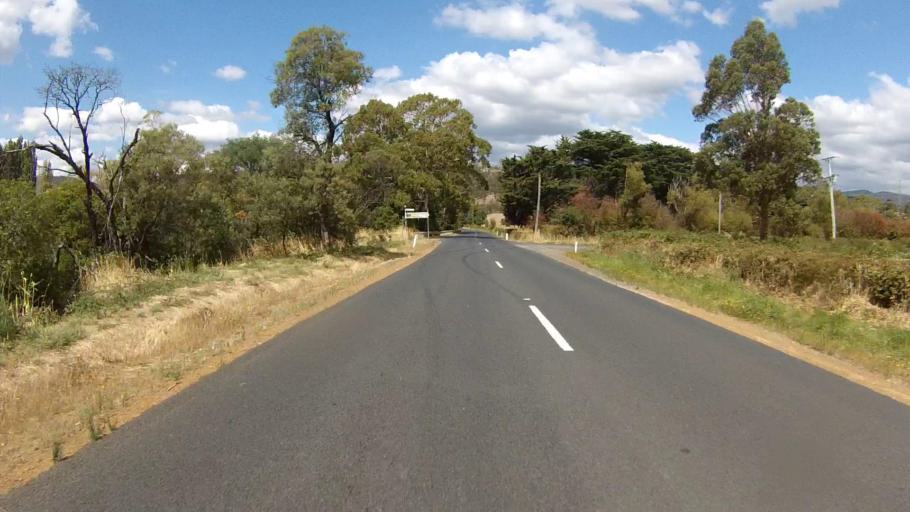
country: AU
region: Tasmania
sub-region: Derwent Valley
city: New Norfolk
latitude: -42.7713
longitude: 147.0272
